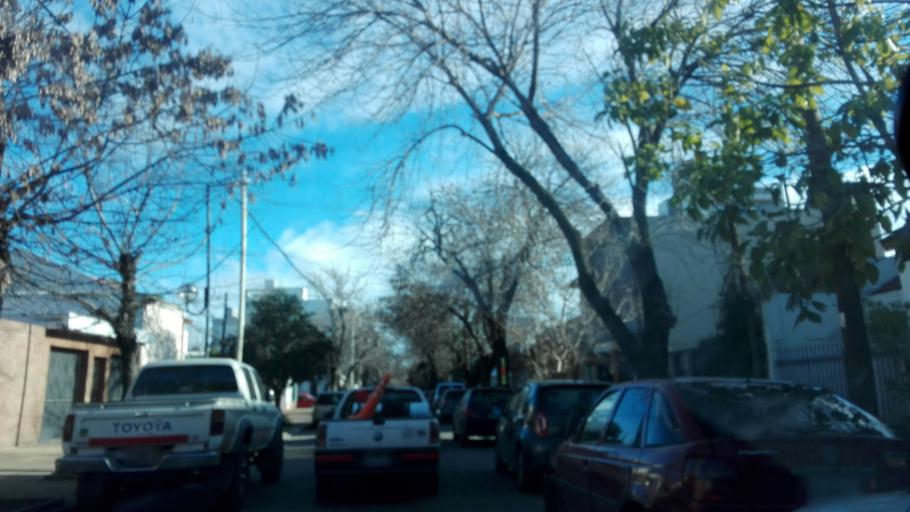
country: AR
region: Buenos Aires
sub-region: Partido de La Plata
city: La Plata
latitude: -34.9289
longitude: -57.9562
